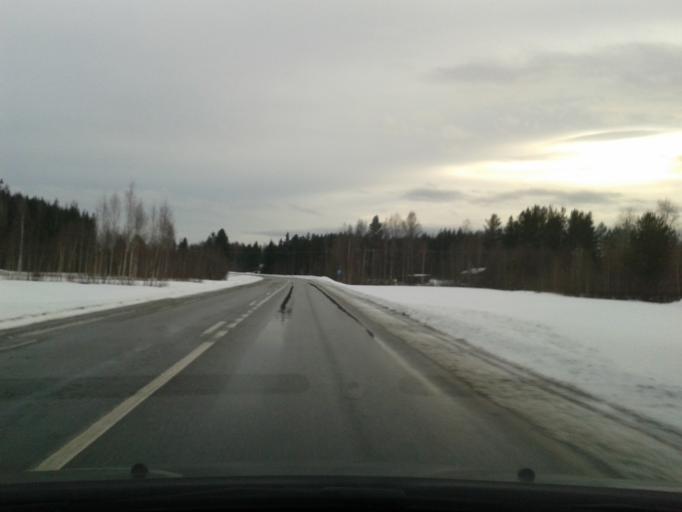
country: SE
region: Vaesternorrland
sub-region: Solleftea Kommun
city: As
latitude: 63.6015
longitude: 16.8184
